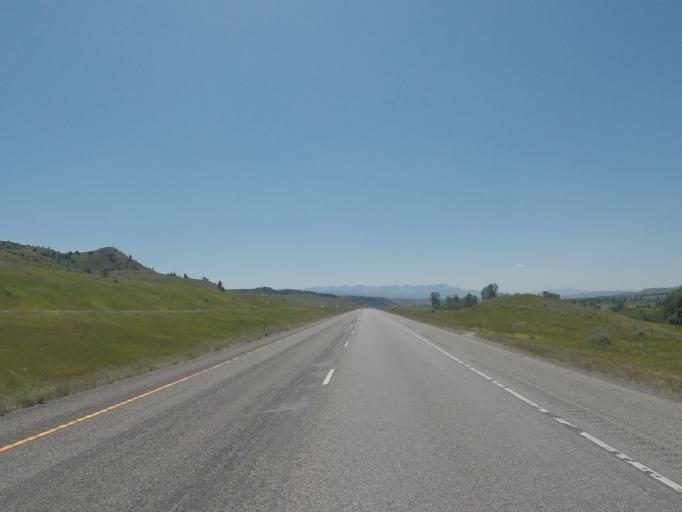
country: US
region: Montana
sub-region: Sweet Grass County
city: Big Timber
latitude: 45.7982
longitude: -110.0321
